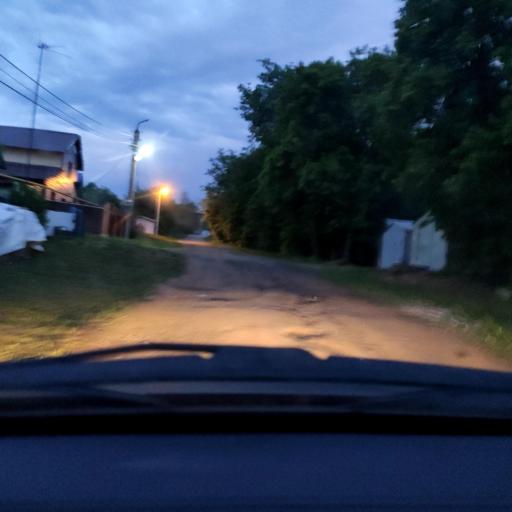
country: RU
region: Bashkortostan
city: Blagoveshchensk
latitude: 54.9019
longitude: 56.1414
